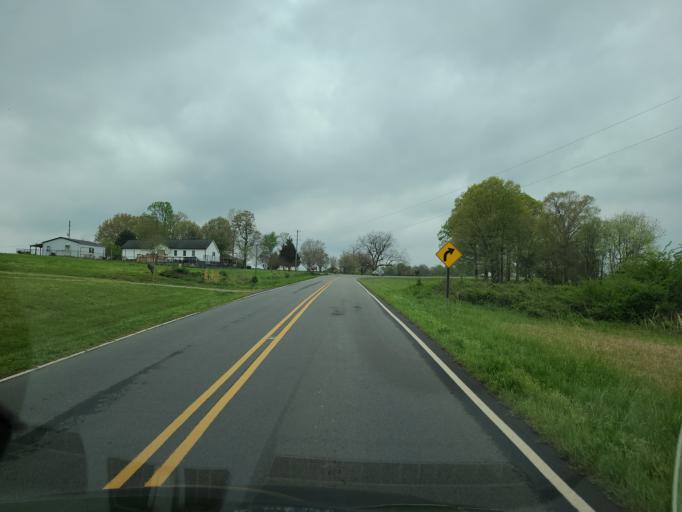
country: US
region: North Carolina
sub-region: Gaston County
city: Cherryville
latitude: 35.4560
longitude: -81.3402
